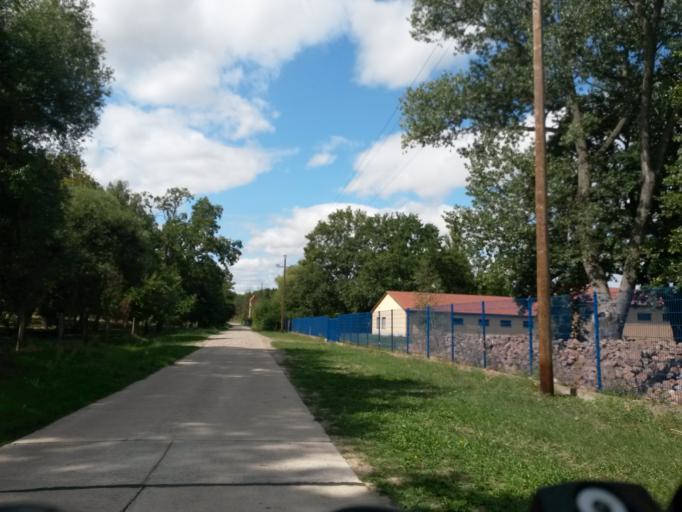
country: DE
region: Saxony-Anhalt
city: Tangermunde
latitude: 52.5082
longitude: 11.9299
